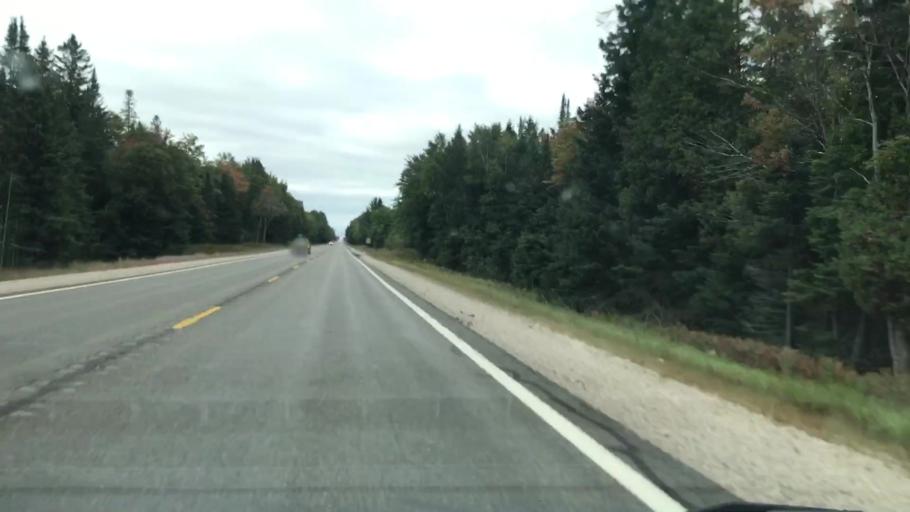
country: US
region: Michigan
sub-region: Luce County
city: Newberry
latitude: 46.2333
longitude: -85.5722
